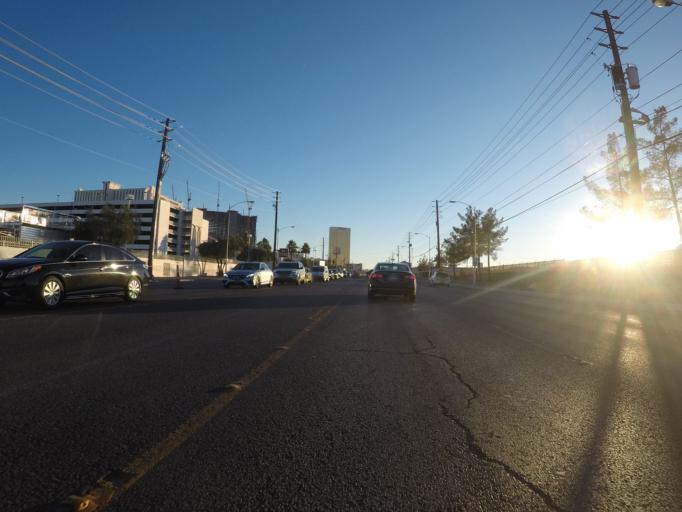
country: US
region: Nevada
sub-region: Clark County
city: Las Vegas
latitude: 36.1428
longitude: -115.1657
